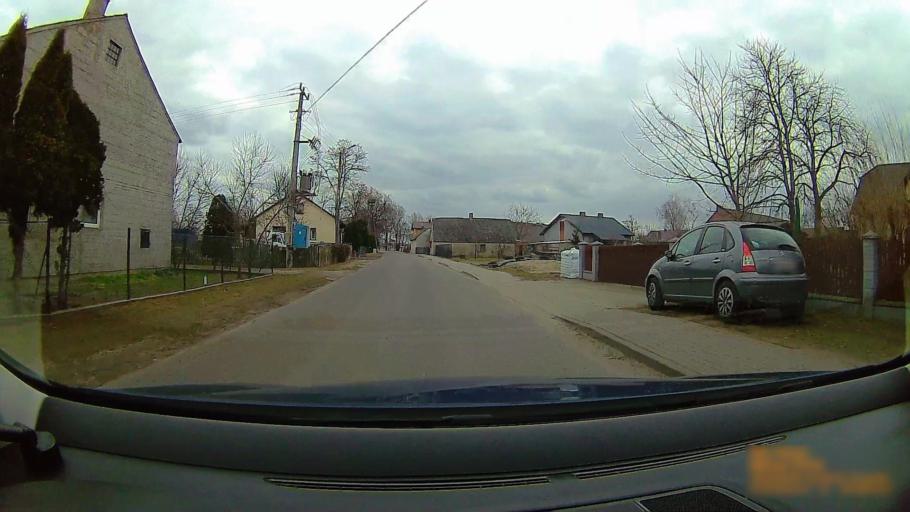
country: PL
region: Greater Poland Voivodeship
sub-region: Powiat koninski
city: Rychwal
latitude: 52.0785
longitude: 18.1367
